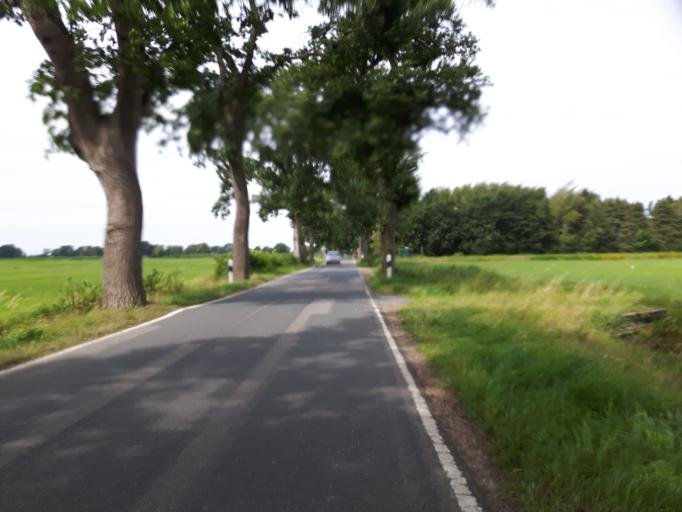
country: DE
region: Lower Saxony
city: Rastede
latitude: 53.2839
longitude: 8.2944
